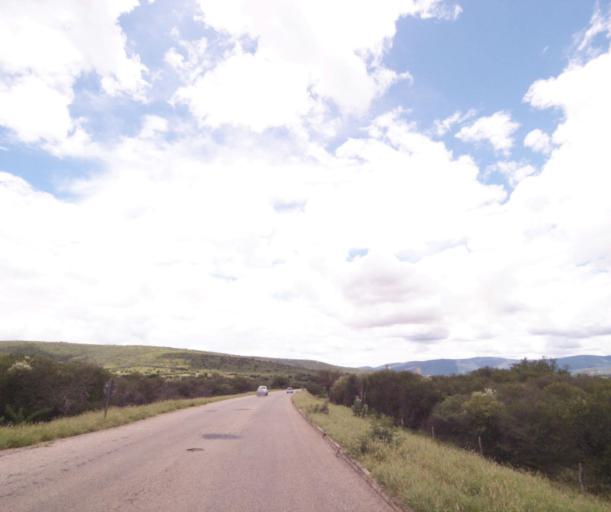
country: BR
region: Bahia
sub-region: Brumado
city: Brumado
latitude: -14.1963
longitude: -41.5835
